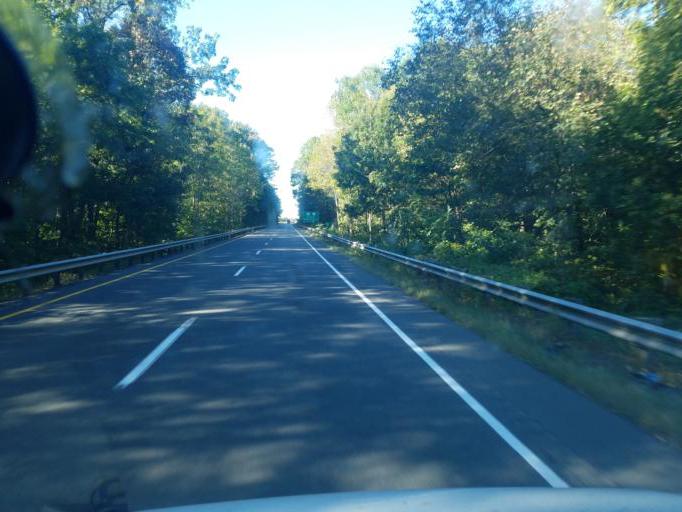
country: US
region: Virginia
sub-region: Culpeper County
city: Culpeper
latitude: 38.4620
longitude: -77.9661
